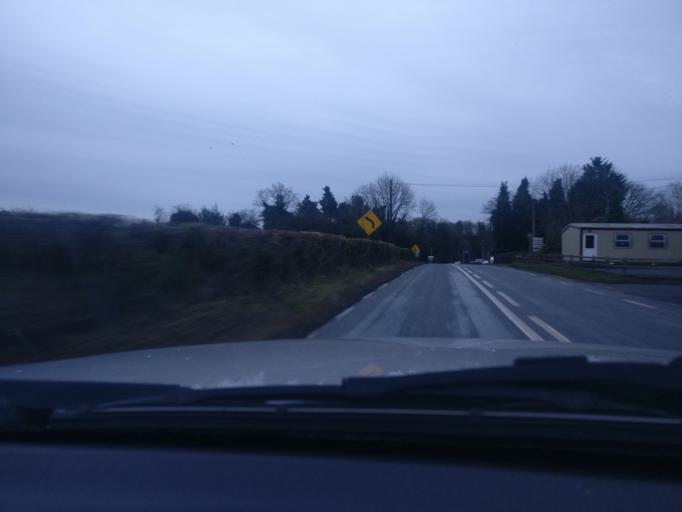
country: IE
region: Leinster
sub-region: An Mhi
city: Navan
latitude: 53.6610
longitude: -6.7239
